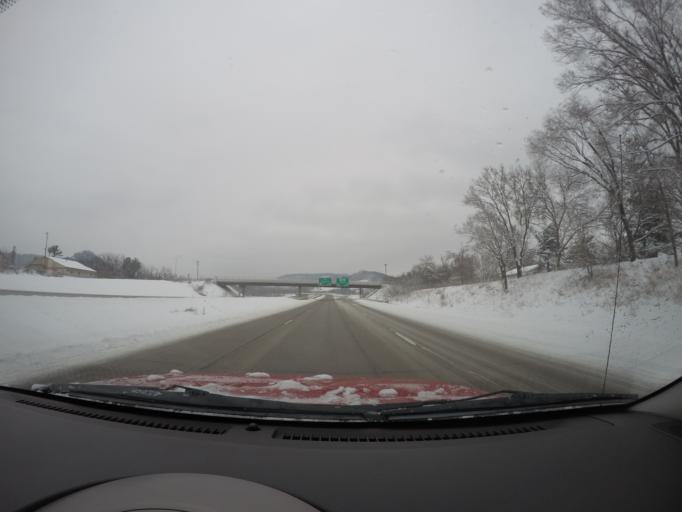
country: US
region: Wisconsin
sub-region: La Crosse County
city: Brice Prairie
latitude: 43.9119
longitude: -91.3606
